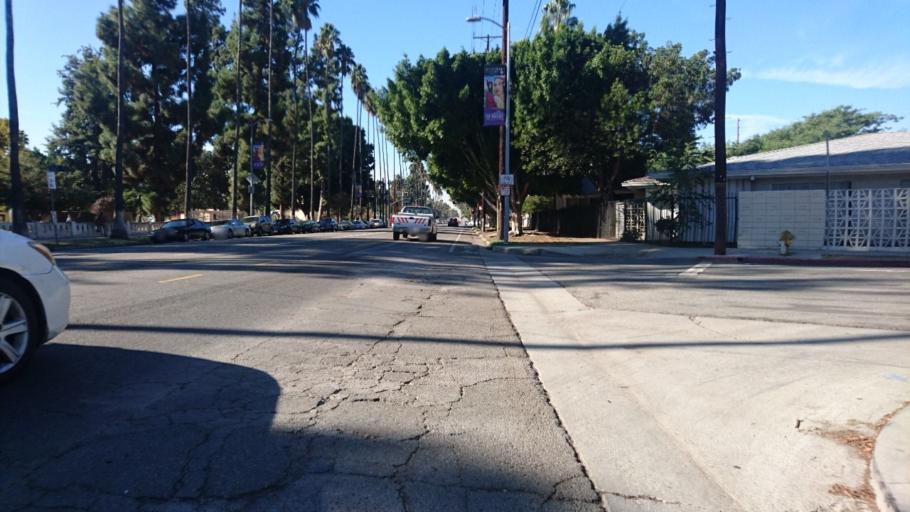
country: US
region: California
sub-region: Los Angeles County
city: Boyle Heights
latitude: 34.0685
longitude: -118.2011
